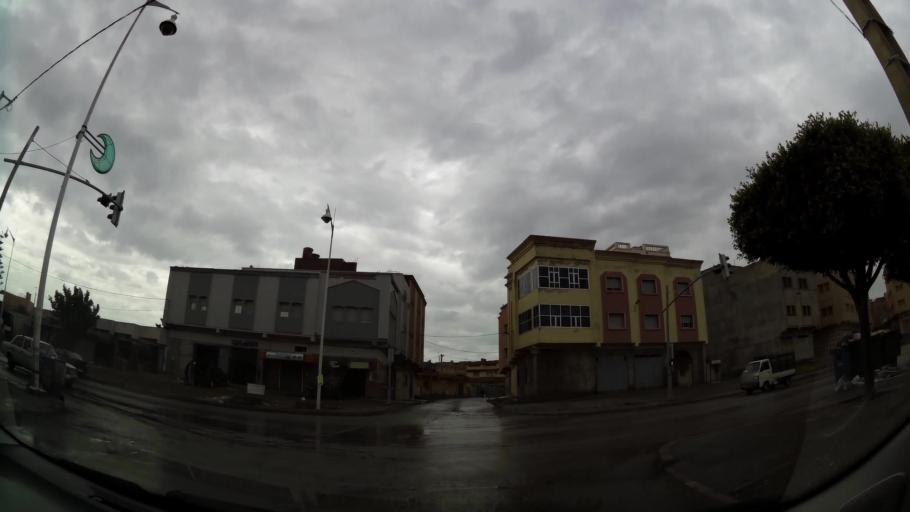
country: MA
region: Oriental
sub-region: Nador
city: Nador
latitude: 35.1512
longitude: -2.9986
